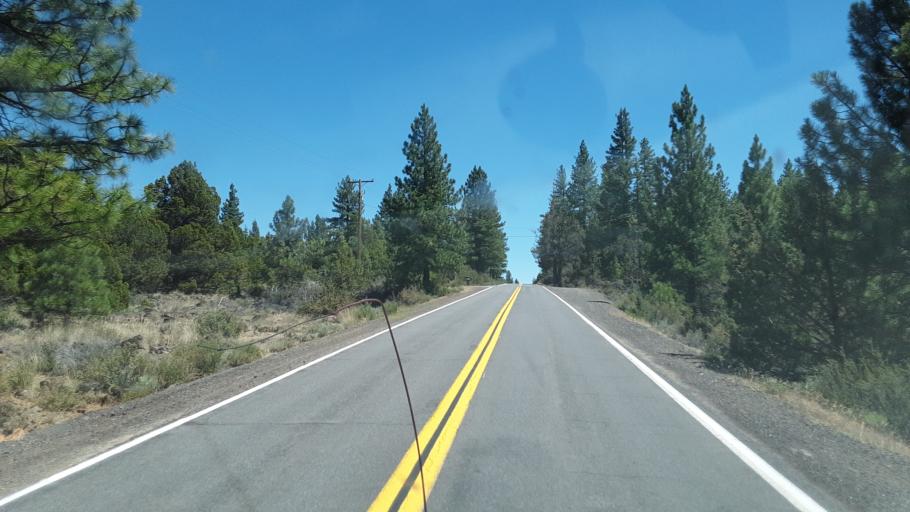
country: US
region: California
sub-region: Lassen County
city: Susanville
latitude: 40.5144
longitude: -120.5769
